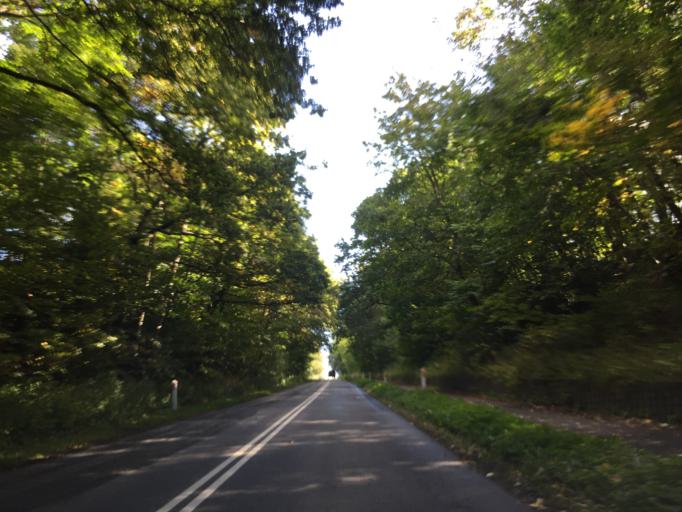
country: DK
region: Central Jutland
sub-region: Viborg Kommune
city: Viborg
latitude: 56.4440
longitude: 9.4620
